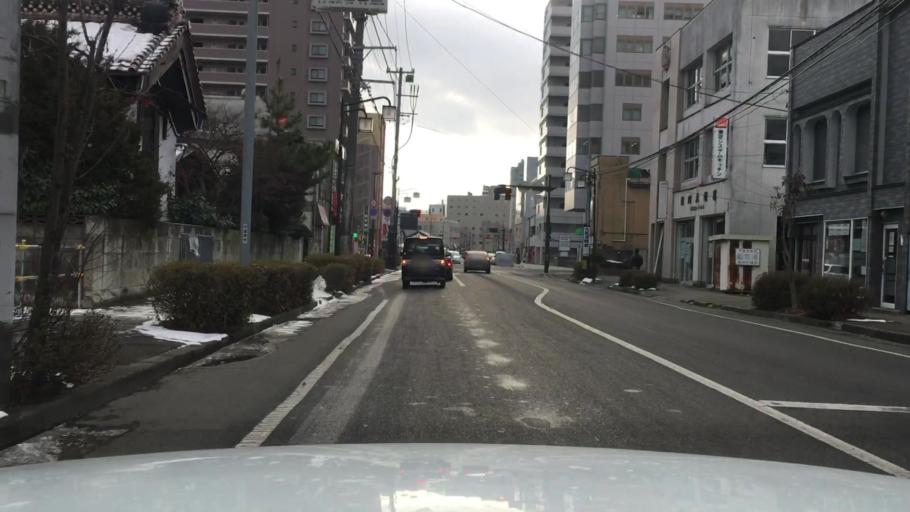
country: JP
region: Iwate
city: Morioka-shi
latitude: 39.7071
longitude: 141.1407
